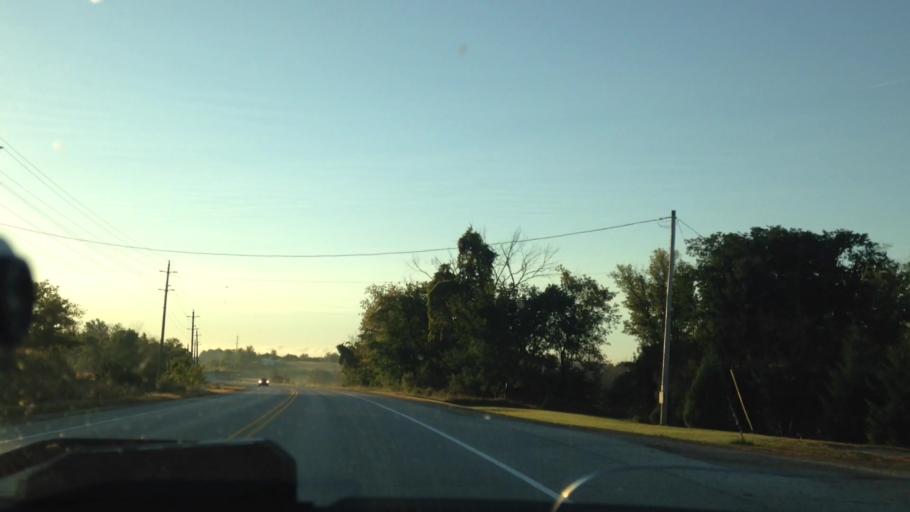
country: US
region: Wisconsin
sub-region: Ozaukee County
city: Saukville
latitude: 43.3912
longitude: -87.9719
